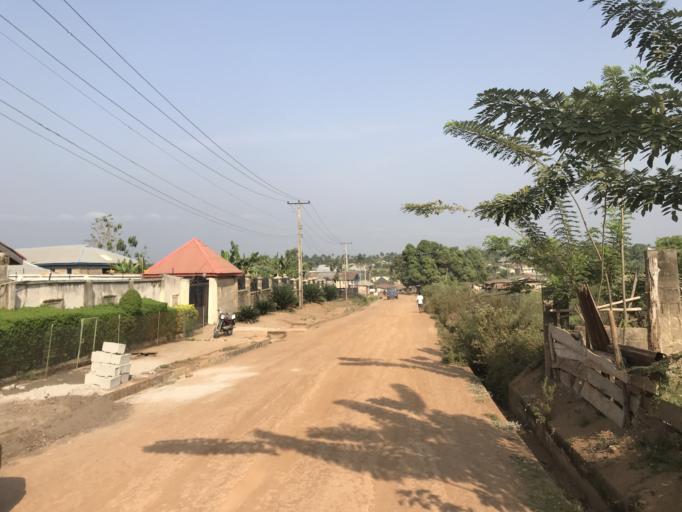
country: NG
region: Osun
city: Iwo
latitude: 7.6199
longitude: 4.1496
